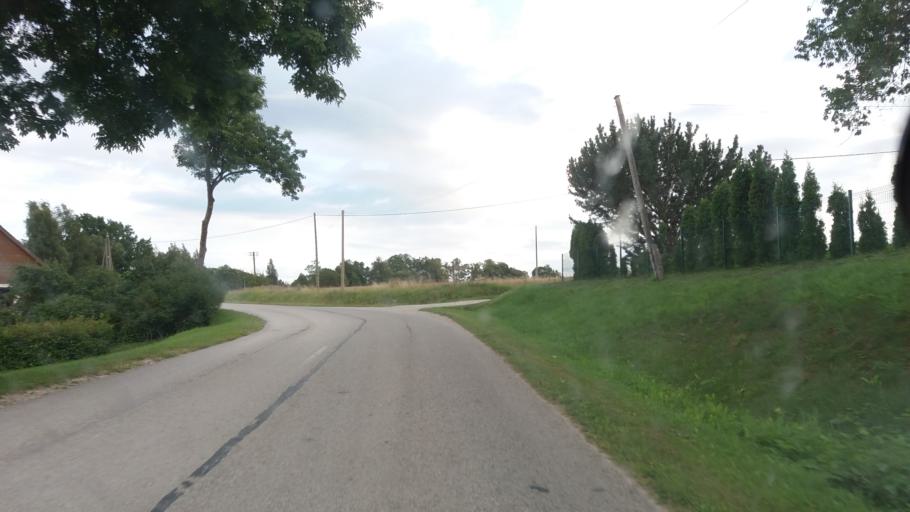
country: LV
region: Talsu Rajons
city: Sabile
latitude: 57.0375
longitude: 22.5713
